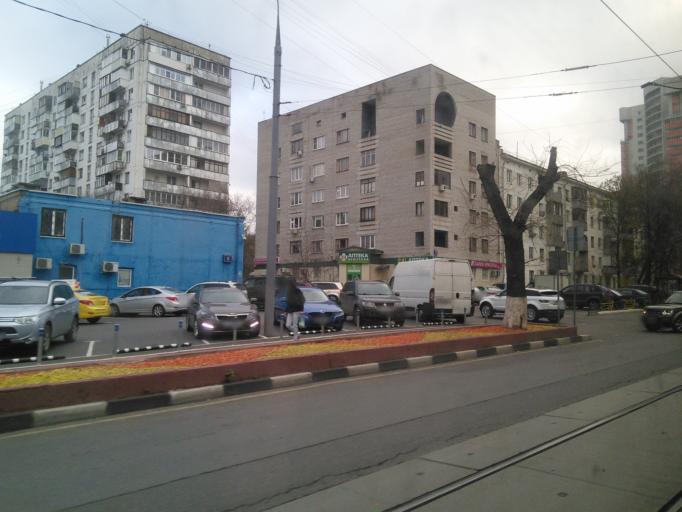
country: RU
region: Moscow
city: Lefortovo
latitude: 55.7615
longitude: 37.7121
